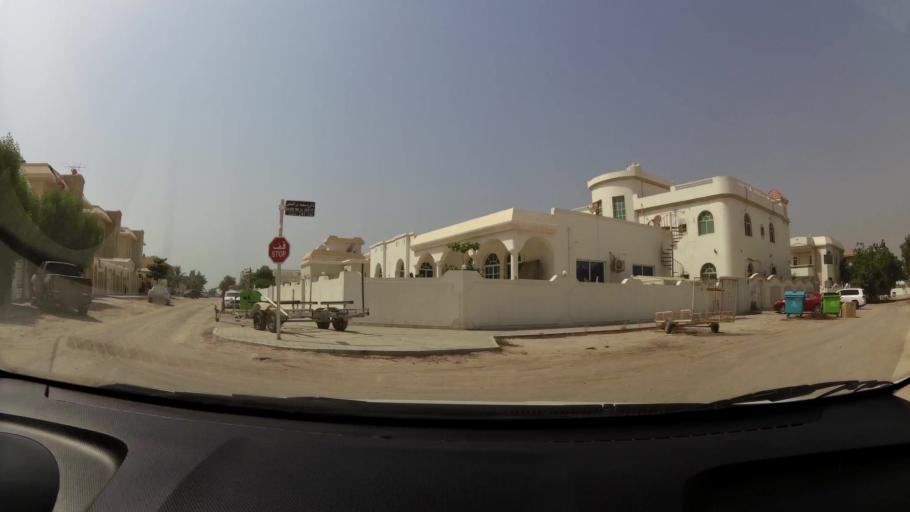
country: AE
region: Ajman
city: Ajman
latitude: 25.3903
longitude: 55.4198
